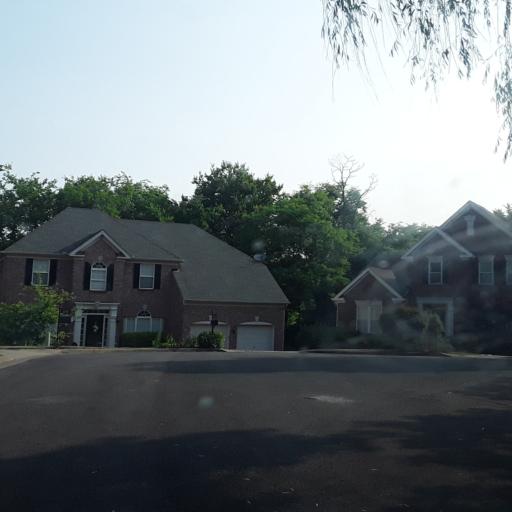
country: US
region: Tennessee
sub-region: Williamson County
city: Brentwood
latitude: 36.0562
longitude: -86.7499
